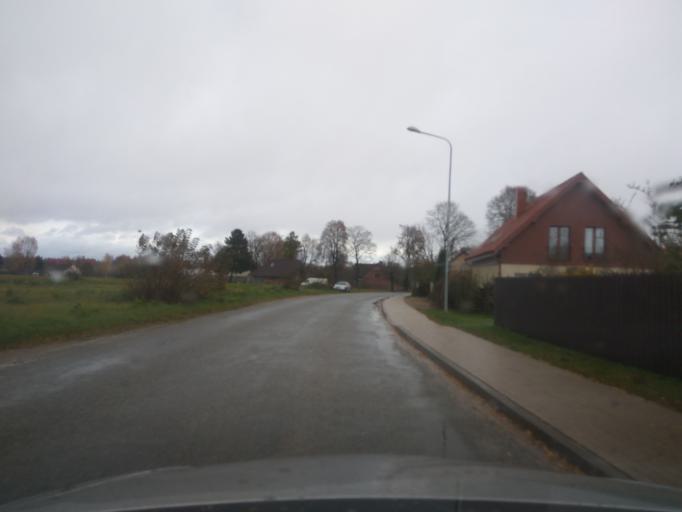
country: LV
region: Kuldigas Rajons
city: Kuldiga
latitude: 56.9708
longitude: 21.9404
